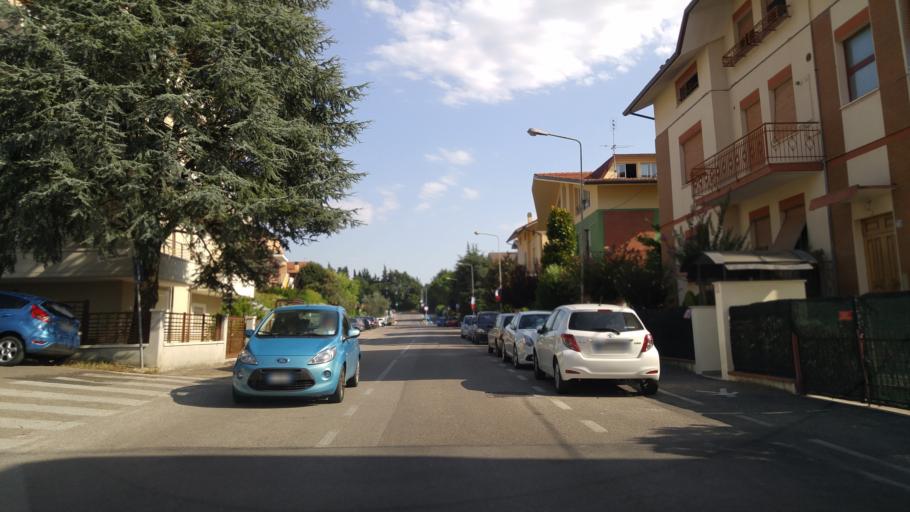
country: IT
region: The Marches
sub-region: Provincia di Pesaro e Urbino
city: Pesaro
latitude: 43.8953
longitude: 12.9243
